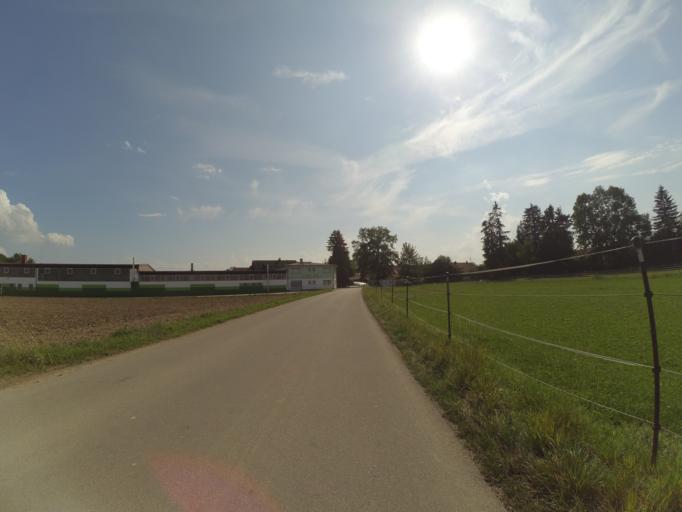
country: DE
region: Bavaria
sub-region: Swabia
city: Lamerdingen
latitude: 48.0881
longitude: 10.7699
